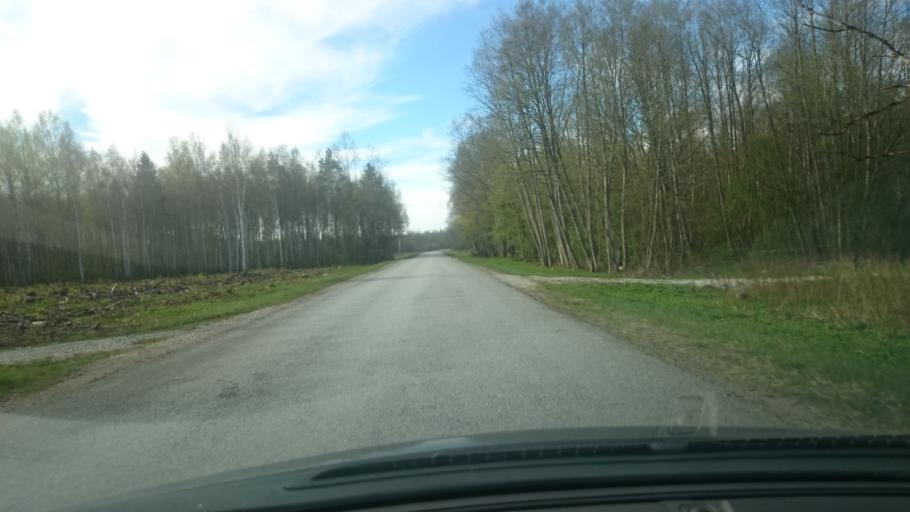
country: EE
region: Ida-Virumaa
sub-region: Sillamaee linn
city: Sillamae
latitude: 59.0913
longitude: 27.6609
